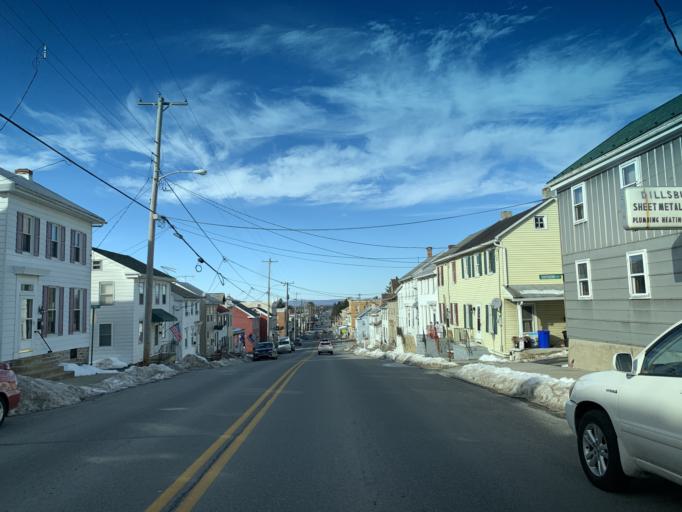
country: US
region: Pennsylvania
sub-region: York County
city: Dillsburg
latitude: 40.1083
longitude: -77.0350
